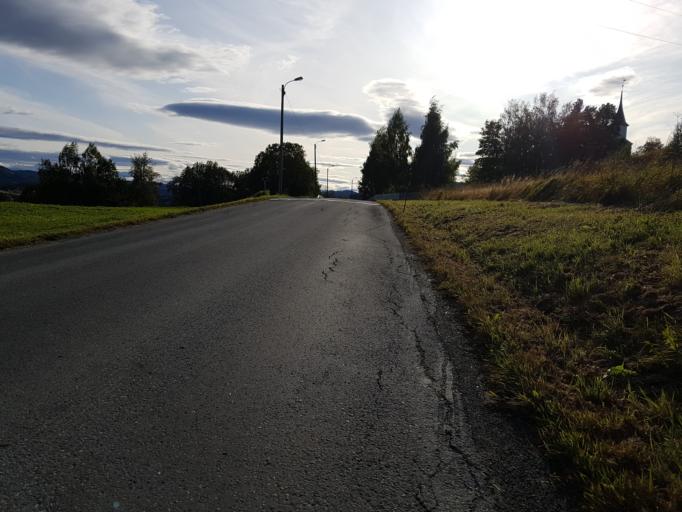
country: NO
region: Sor-Trondelag
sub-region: Klaebu
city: Klaebu
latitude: 63.3488
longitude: 10.4841
